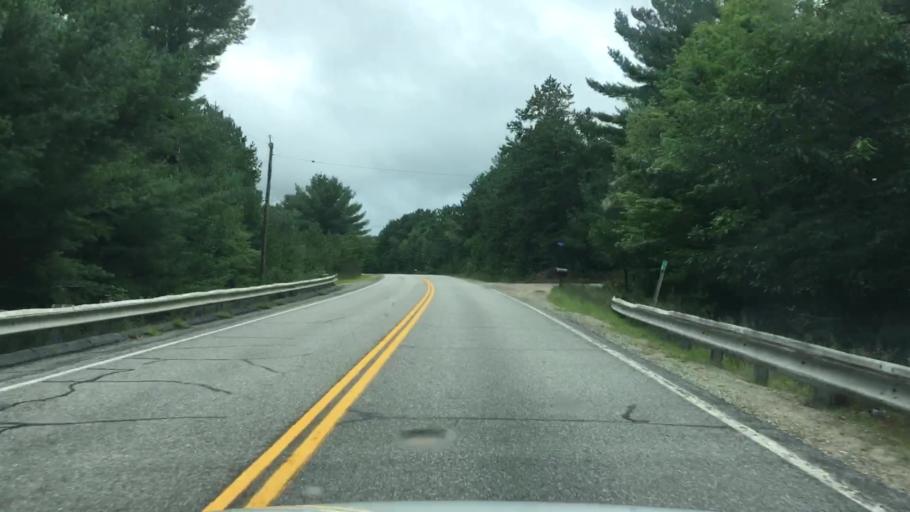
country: US
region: Maine
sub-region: Oxford County
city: Hiram
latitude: 43.9065
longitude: -70.8459
